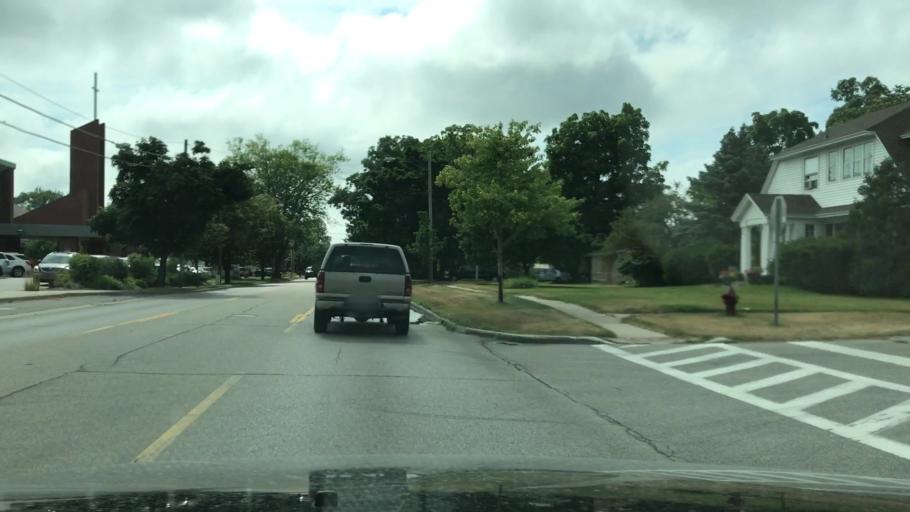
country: US
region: Michigan
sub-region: Ottawa County
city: Spring Lake
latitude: 43.0767
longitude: -86.1889
